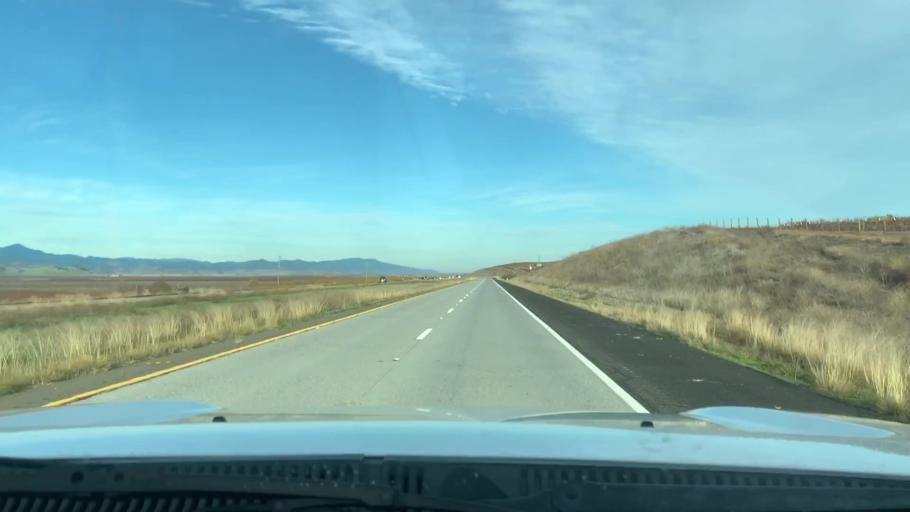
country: US
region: California
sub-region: Monterey County
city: King City
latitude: 36.0668
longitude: -120.9851
